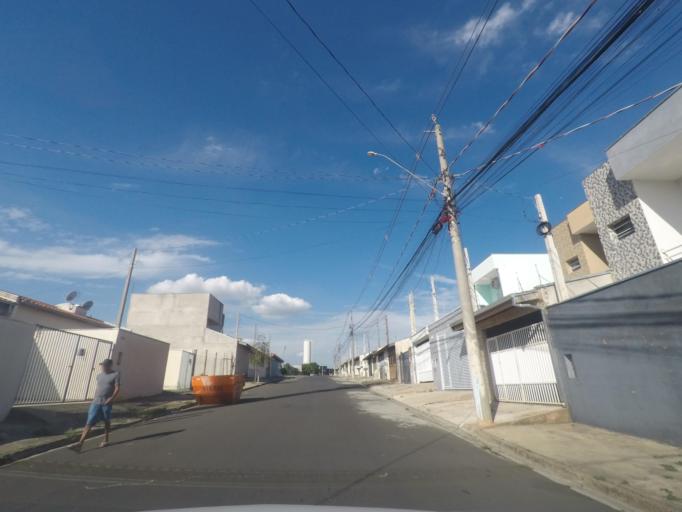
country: BR
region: Sao Paulo
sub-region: Sumare
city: Sumare
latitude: -22.8052
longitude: -47.2729
